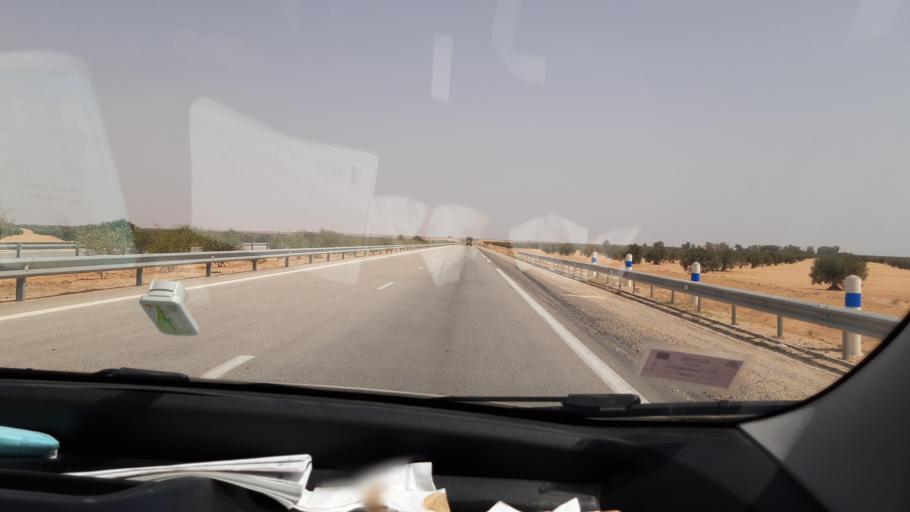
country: TN
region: Safaqis
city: Bi'r `Ali Bin Khalifah
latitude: 34.5307
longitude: 10.1030
